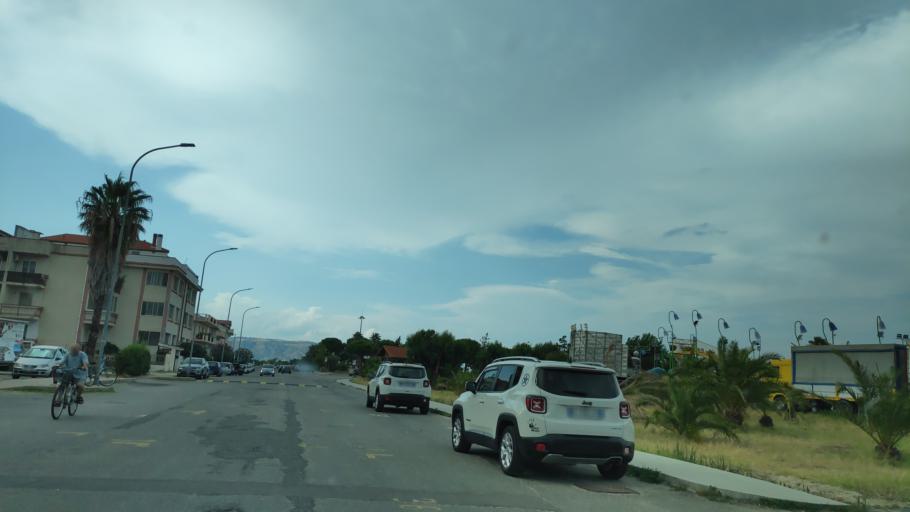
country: IT
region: Calabria
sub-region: Provincia di Catanzaro
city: Soverato Marina
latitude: 38.6837
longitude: 16.5556
